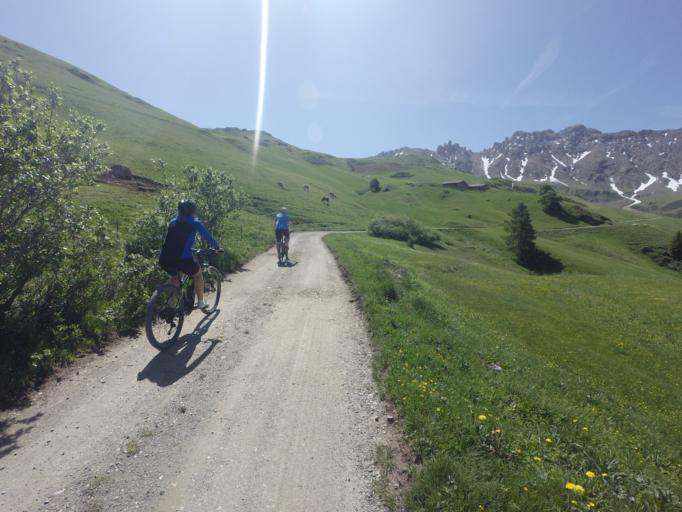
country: IT
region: Trentino-Alto Adige
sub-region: Bolzano
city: Ortisei
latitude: 46.5167
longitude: 11.6289
